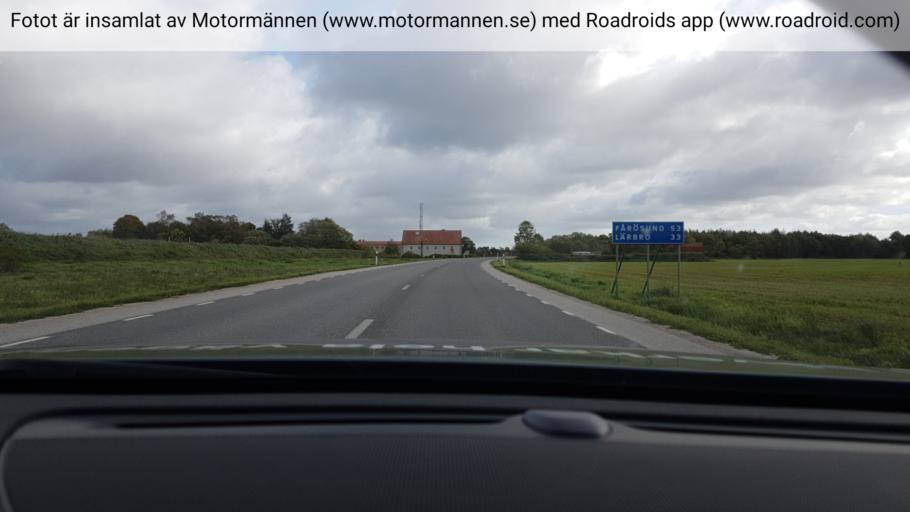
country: SE
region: Gotland
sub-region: Gotland
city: Visby
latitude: 57.6452
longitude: 18.3422
